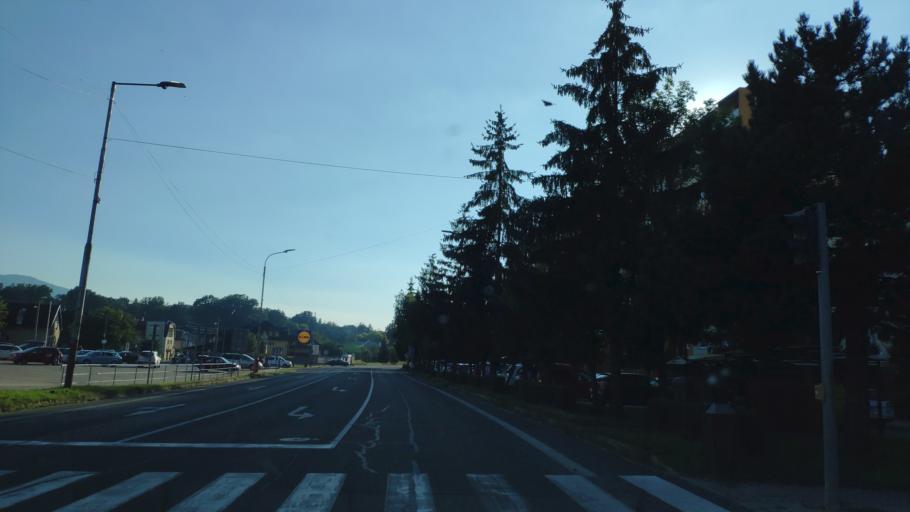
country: SK
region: Presovsky
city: Snina
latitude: 48.9876
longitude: 22.1556
